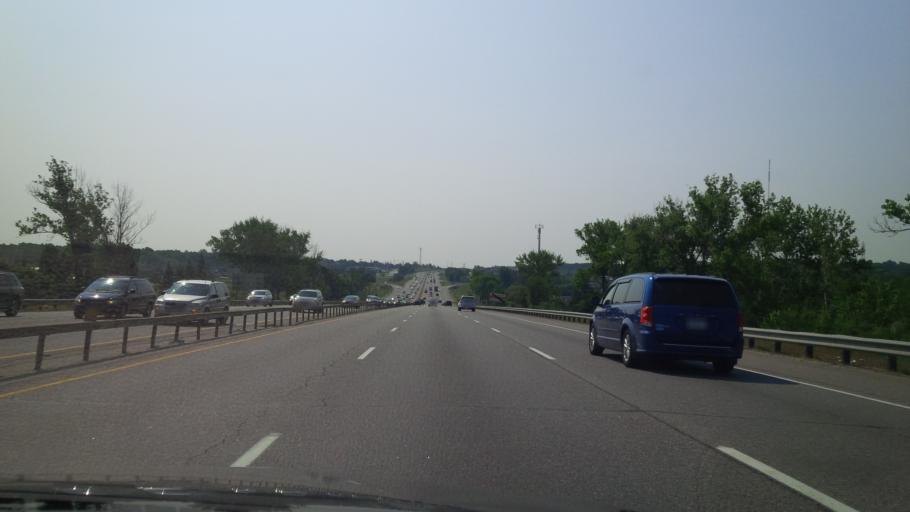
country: CA
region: Ontario
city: Barrie
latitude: 44.3691
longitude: -79.7056
